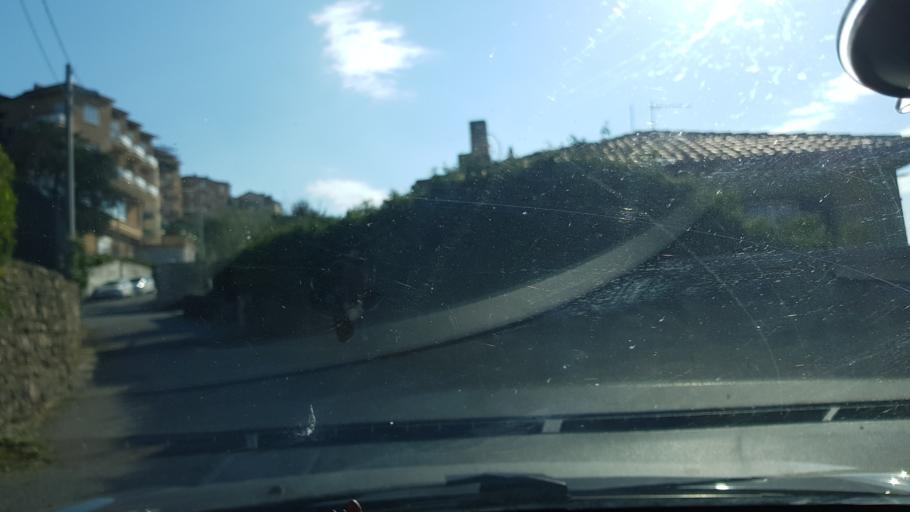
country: IT
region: Friuli Venezia Giulia
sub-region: Provincia di Trieste
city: Trieste
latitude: 45.6443
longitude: 13.8005
